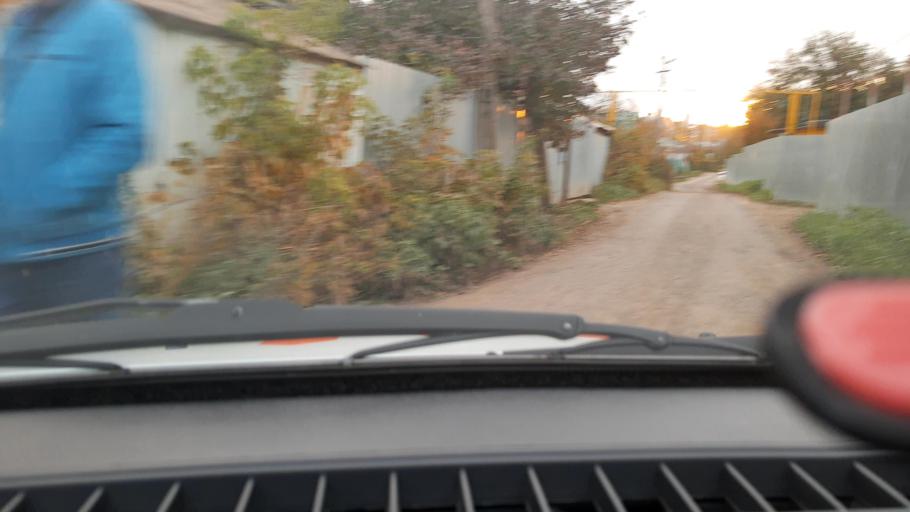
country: RU
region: Bashkortostan
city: Ufa
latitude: 54.7060
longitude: 55.9474
